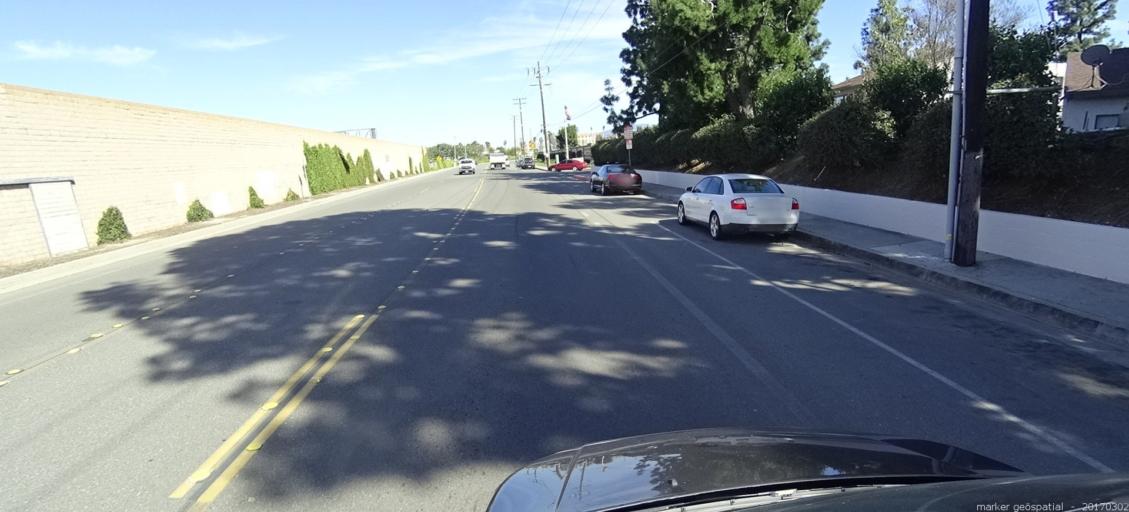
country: US
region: California
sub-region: Orange County
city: Placentia
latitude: 33.8463
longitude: -117.8600
